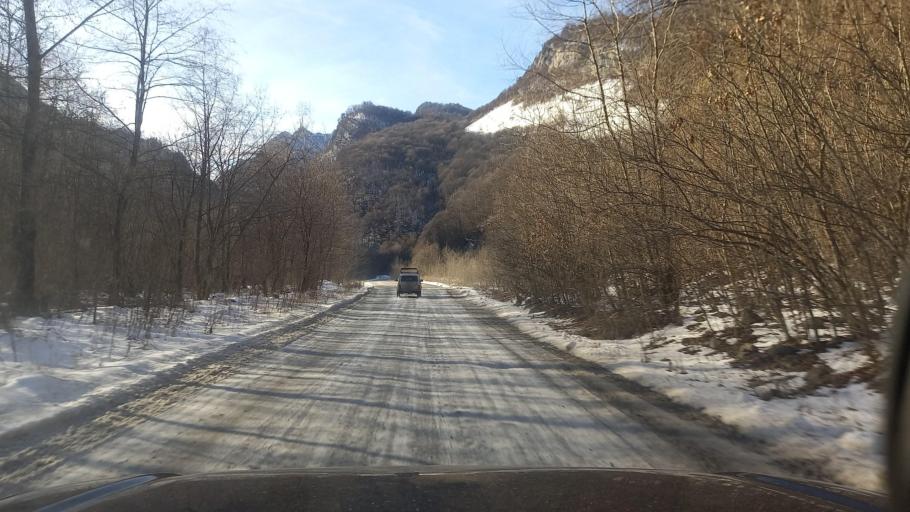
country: RU
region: North Ossetia
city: Gizel'
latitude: 42.9144
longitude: 44.5349
